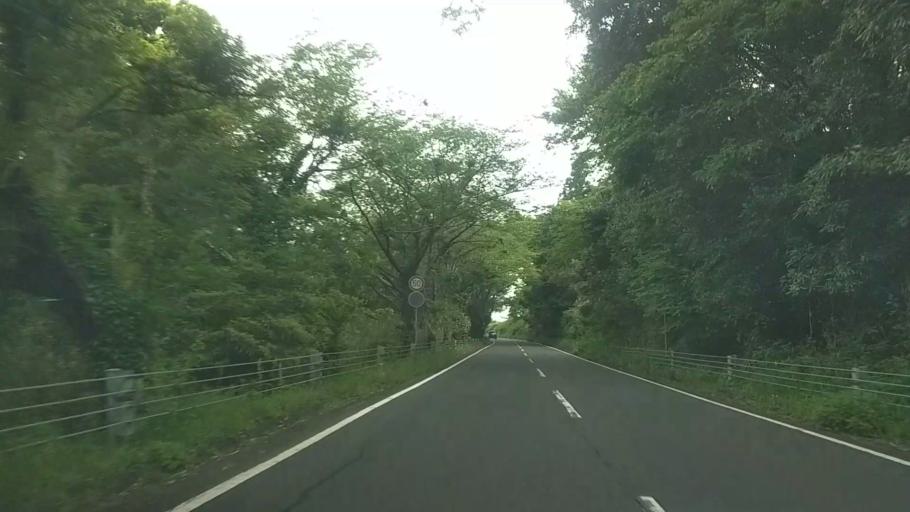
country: JP
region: Shizuoka
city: Kosai-shi
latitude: 34.7427
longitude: 137.5979
